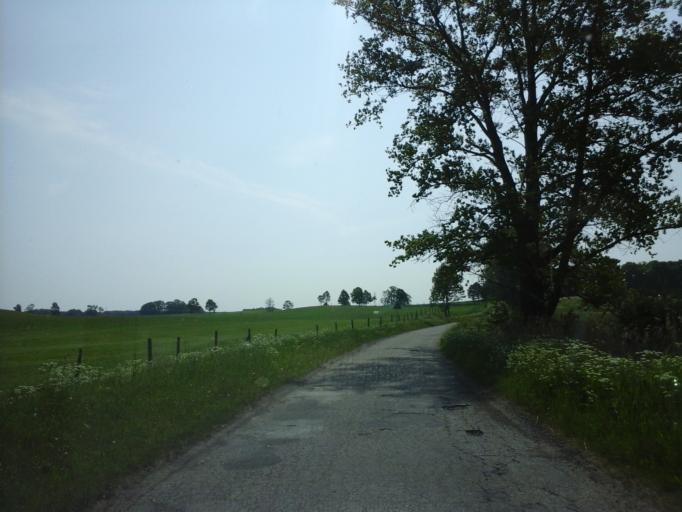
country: PL
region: West Pomeranian Voivodeship
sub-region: Powiat choszczenski
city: Recz
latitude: 53.3476
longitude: 15.5477
